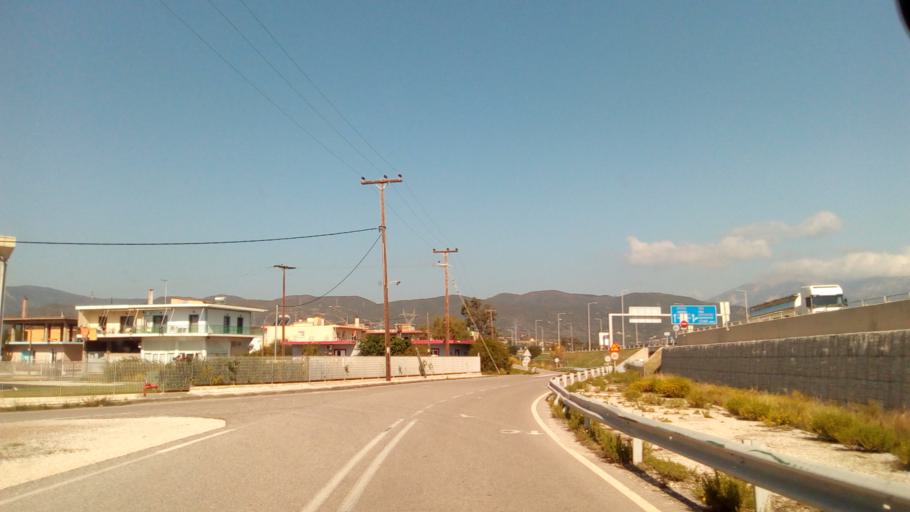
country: GR
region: West Greece
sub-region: Nomos Aitolias kai Akarnanias
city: Antirrio
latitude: 38.3341
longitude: 21.7651
